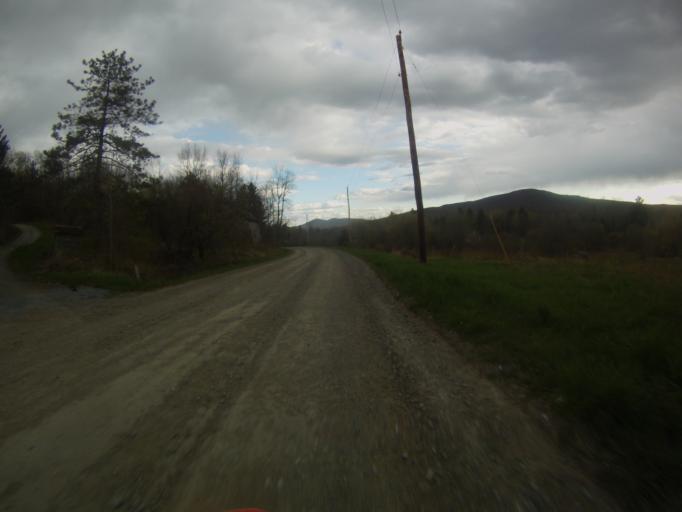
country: US
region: Vermont
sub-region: Addison County
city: Bristol
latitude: 44.0433
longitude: -73.0148
